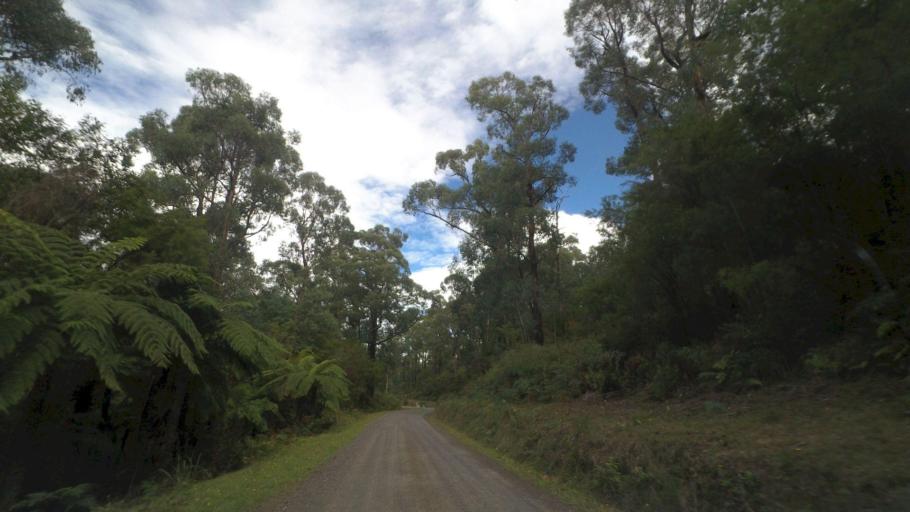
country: AU
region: Victoria
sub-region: Cardinia
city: Bunyip
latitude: -37.9886
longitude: 145.8136
